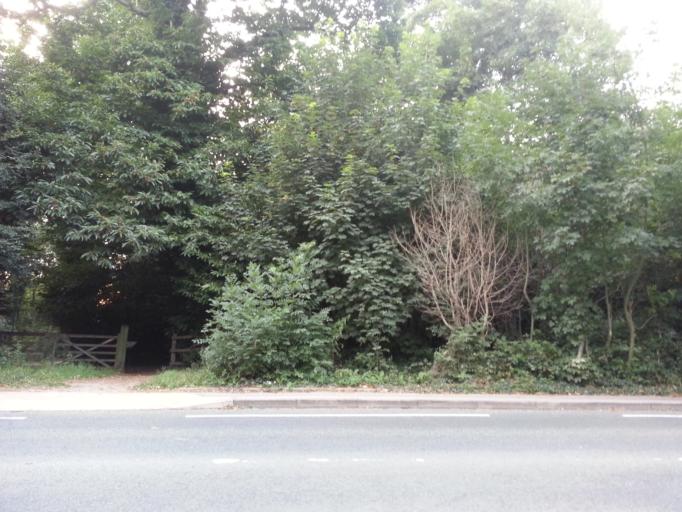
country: GB
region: England
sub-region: Suffolk
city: Ipswich
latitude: 52.0342
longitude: 1.1345
